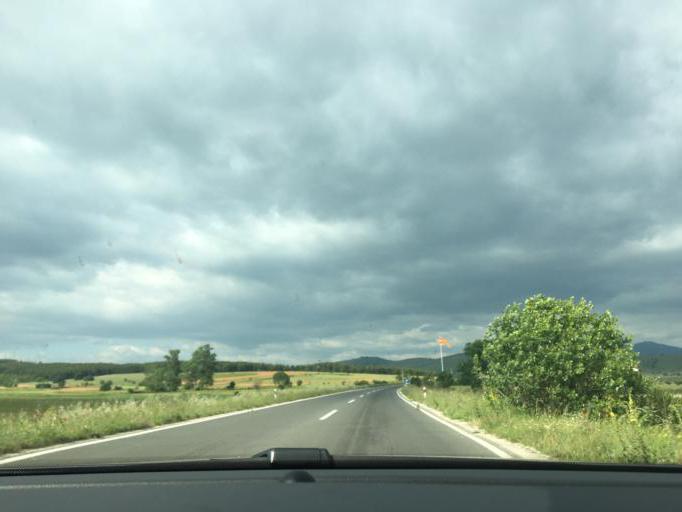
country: MK
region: Prilep
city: Topolcani
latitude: 41.2682
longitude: 21.4747
